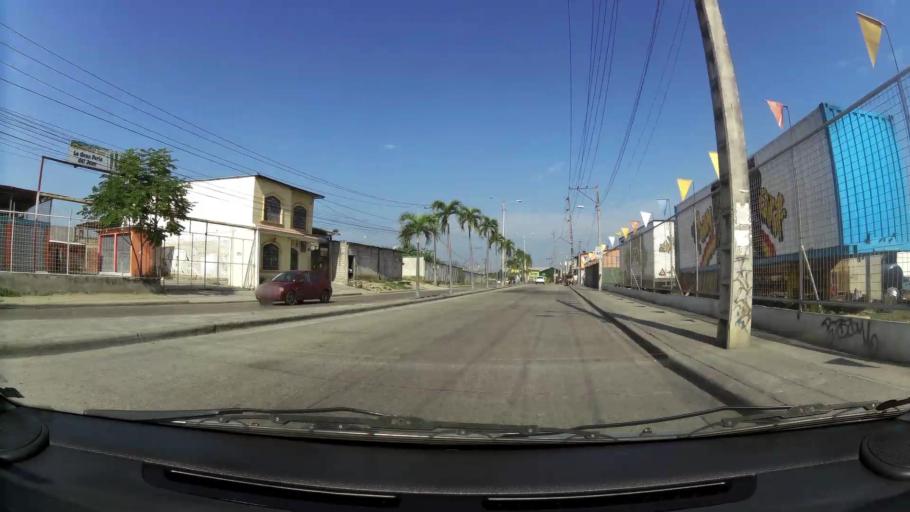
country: EC
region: Guayas
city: Eloy Alfaro
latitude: -2.0962
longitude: -79.9124
